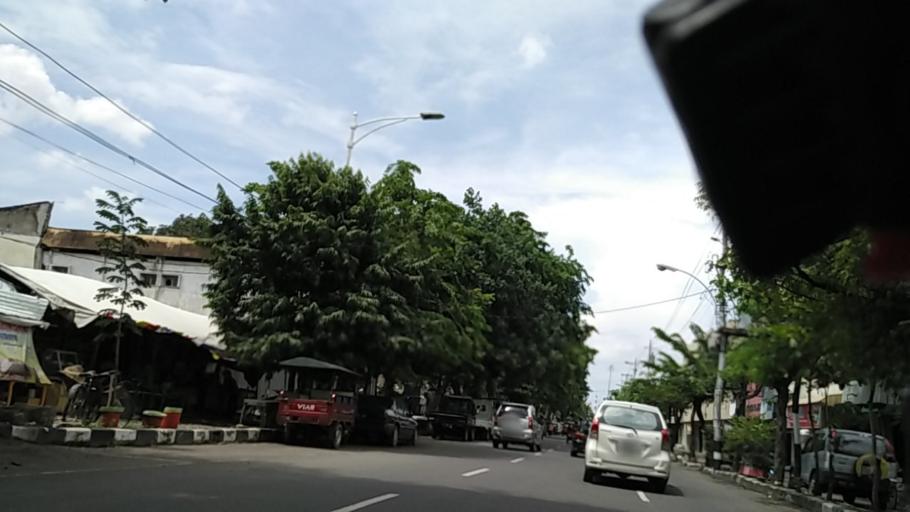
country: ID
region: Central Java
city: Semarang
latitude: -6.9734
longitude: 110.4312
